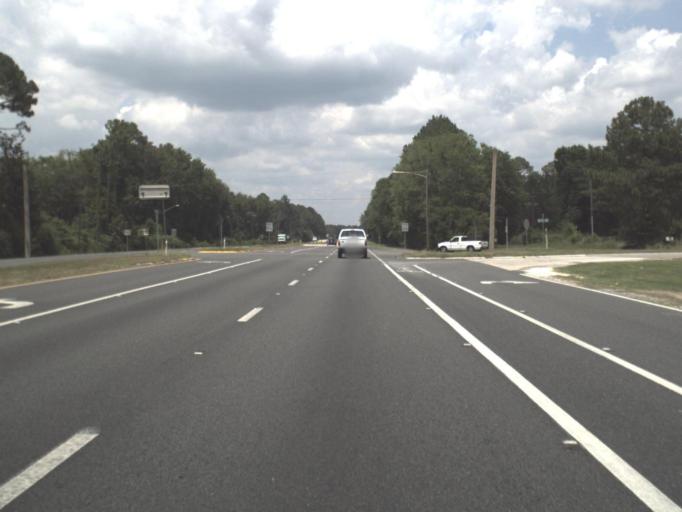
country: US
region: Florida
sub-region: Alachua County
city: Gainesville
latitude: 29.7041
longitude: -82.2762
